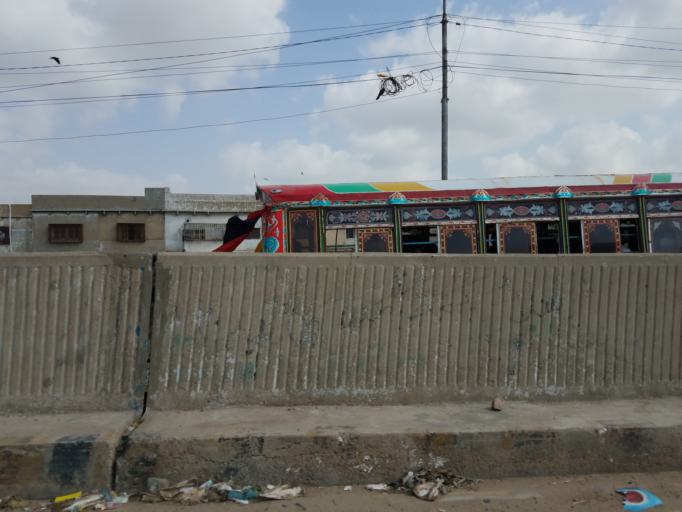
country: PK
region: Sindh
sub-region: Karachi District
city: Karachi
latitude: 24.9166
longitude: 67.0522
